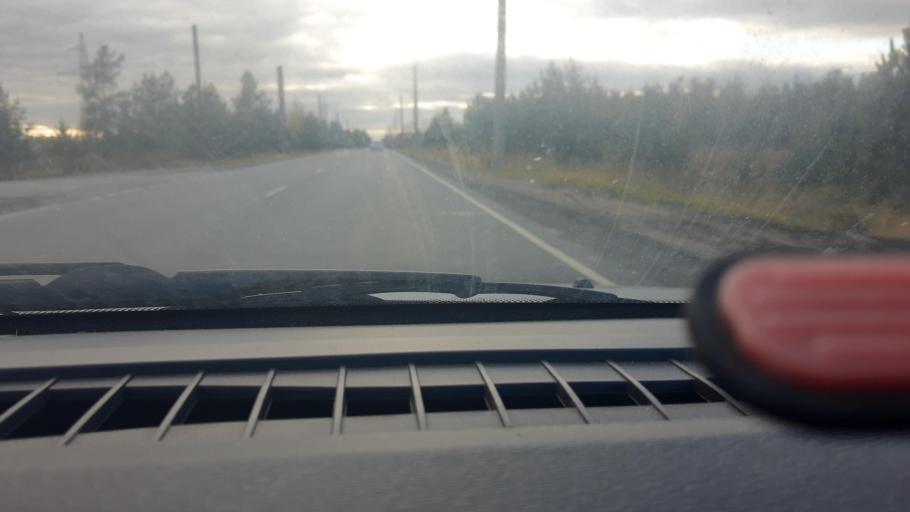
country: RU
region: Nizjnij Novgorod
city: Babino
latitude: 56.2717
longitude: 43.5467
